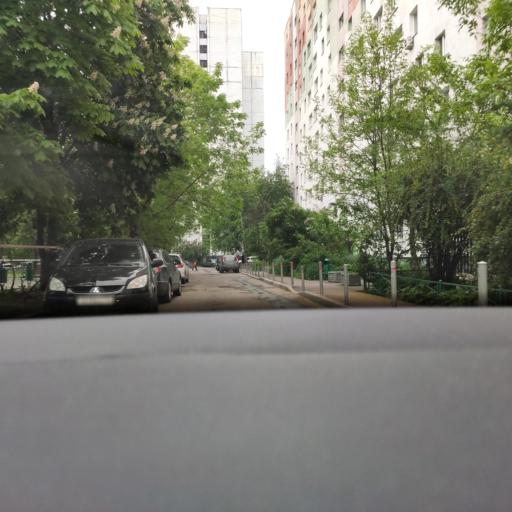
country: RU
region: Moscow
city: Vagonoremont
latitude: 55.8970
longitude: 37.5642
